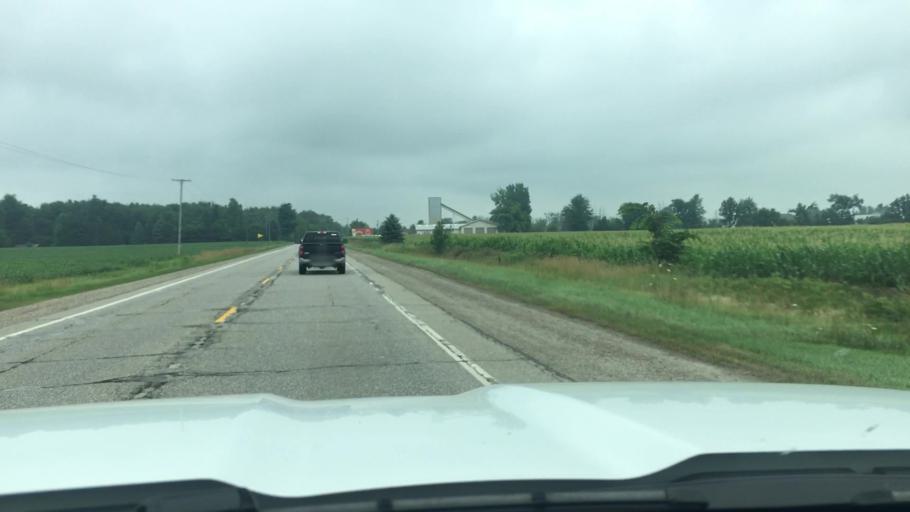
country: US
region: Michigan
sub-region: Sanilac County
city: Marlette
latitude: 43.2441
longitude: -83.0787
